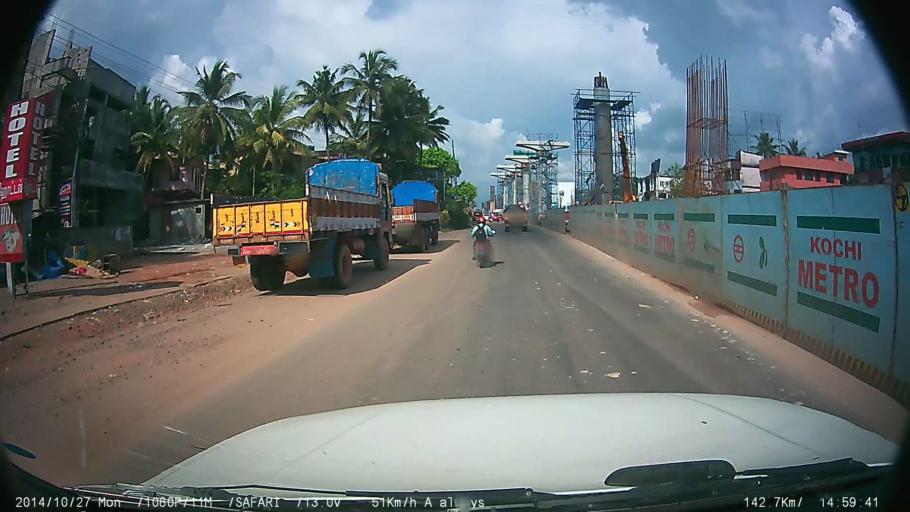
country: IN
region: Kerala
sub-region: Ernakulam
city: Aluva
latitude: 10.0710
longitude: 76.3321
